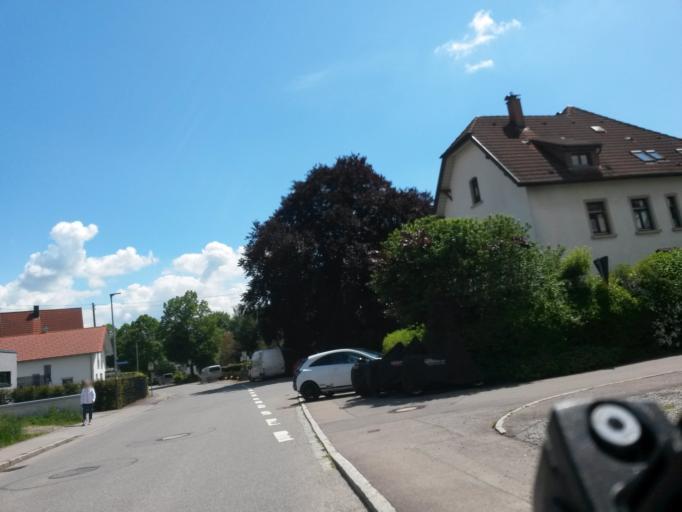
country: DE
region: Baden-Wuerttemberg
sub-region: Tuebingen Region
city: Bad Waldsee
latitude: 47.9278
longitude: 9.7471
